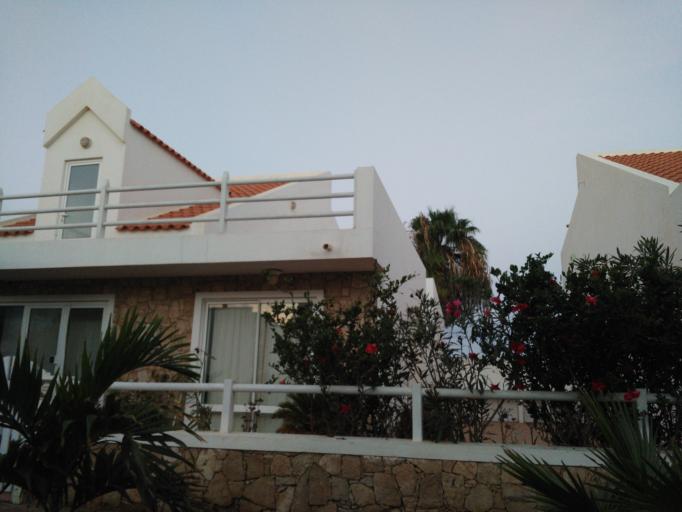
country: CV
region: Sal
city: Espargos
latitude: 16.6754
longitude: -22.9348
